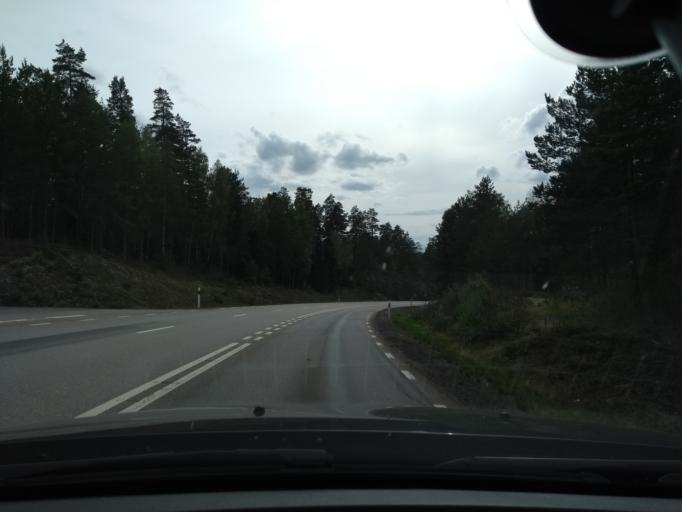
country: SE
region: Joenkoeping
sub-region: Eksjo Kommun
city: Mariannelund
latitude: 57.6280
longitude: 15.6183
